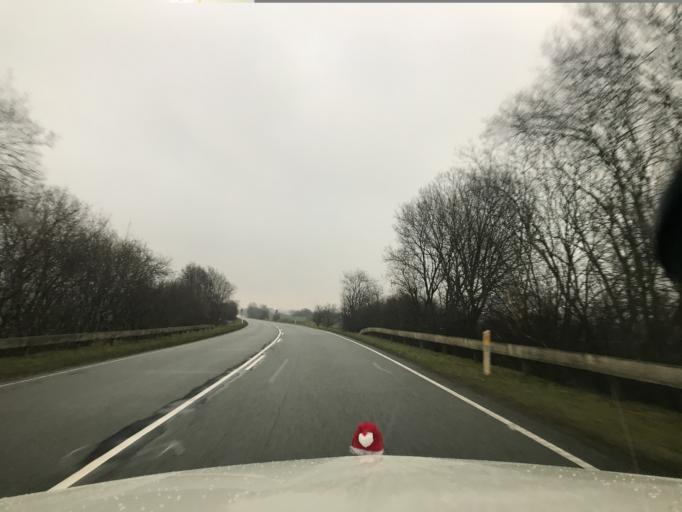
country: DK
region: South Denmark
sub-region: Aabenraa Kommune
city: Aabenraa
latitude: 55.0008
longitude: 9.3722
